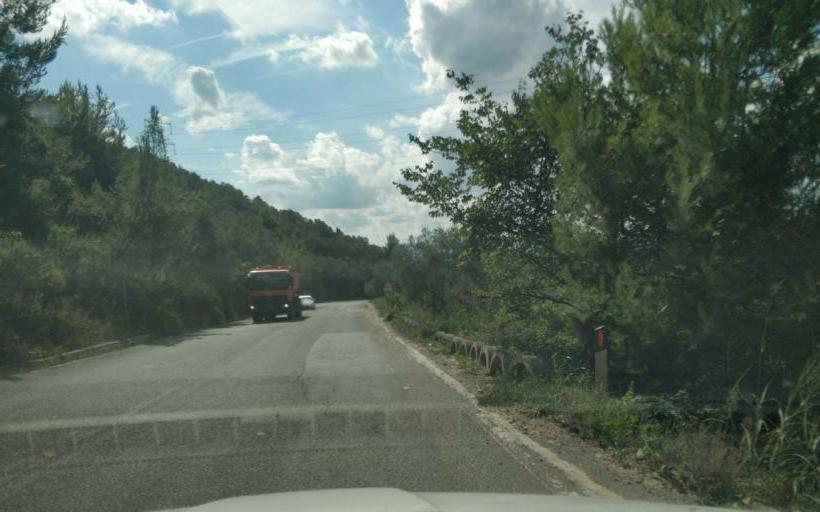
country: AL
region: Durres
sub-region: Rrethi i Krujes
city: Kruje
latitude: 41.4864
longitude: 19.7670
